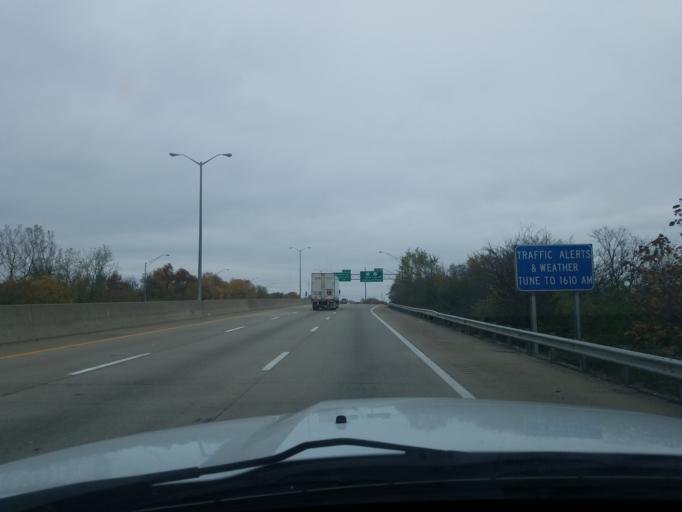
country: US
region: Kentucky
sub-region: Jefferson County
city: Shively
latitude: 38.2185
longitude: -85.8223
